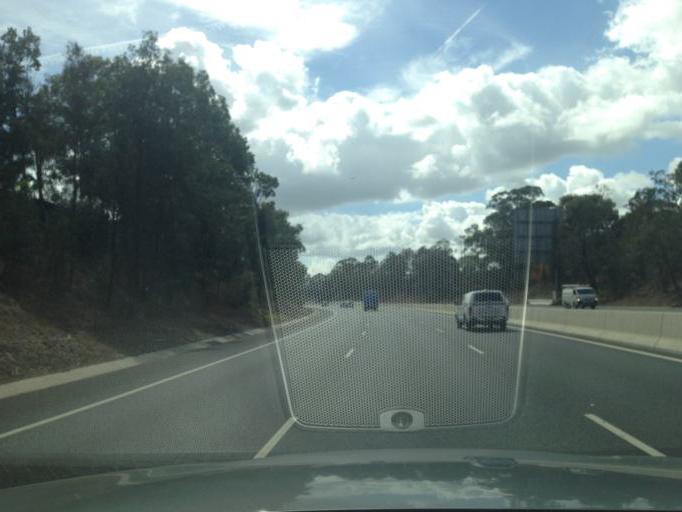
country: AU
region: New South Wales
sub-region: Bankstown
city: Milperra
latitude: -33.9436
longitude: 150.9969
